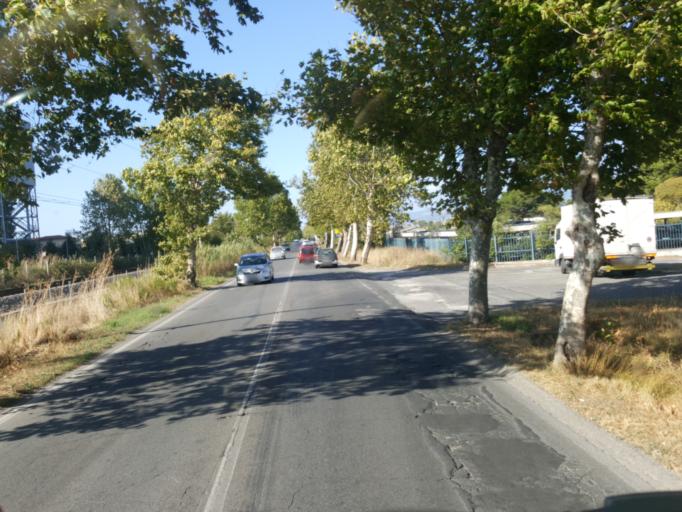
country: IT
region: Latium
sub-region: Provincia di Latina
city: Campo di Carne
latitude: 41.5603
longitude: 12.6359
